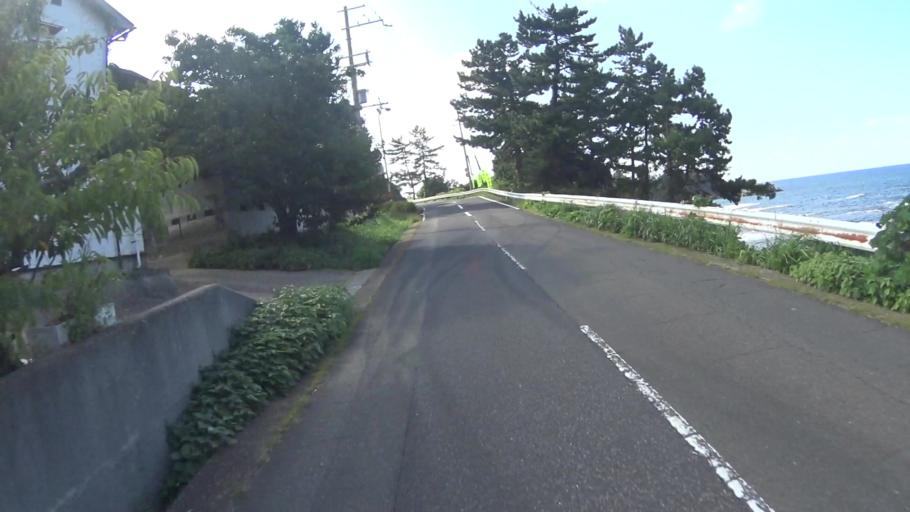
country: JP
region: Kyoto
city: Miyazu
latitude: 35.7644
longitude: 135.2012
